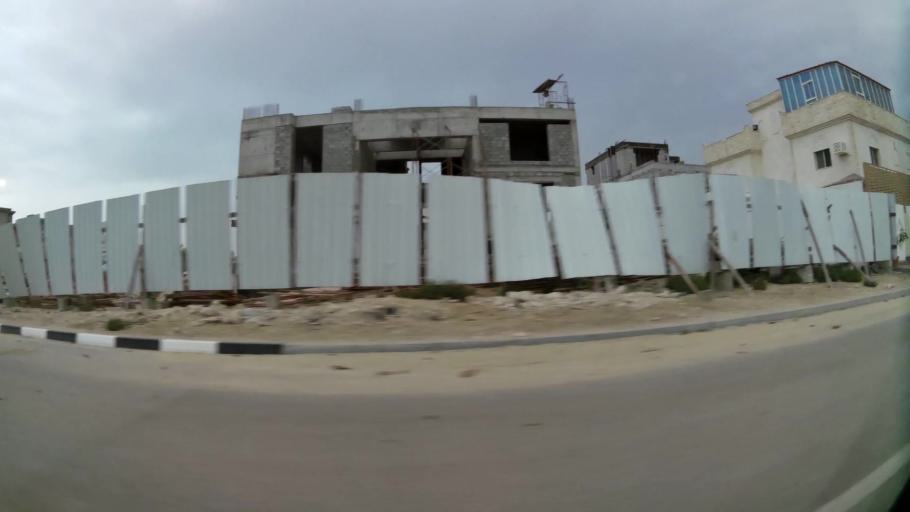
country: QA
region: Baladiyat ad Dawhah
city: Doha
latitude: 25.3494
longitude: 51.5121
